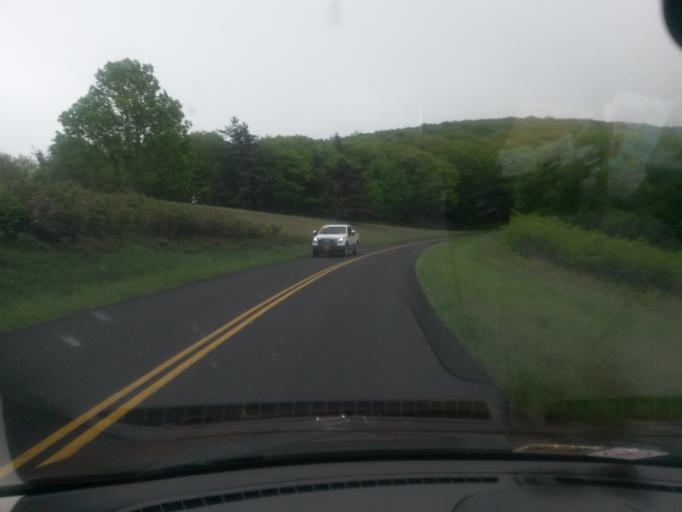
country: US
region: Virginia
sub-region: Floyd County
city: Floyd
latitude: 36.8235
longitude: -80.3427
